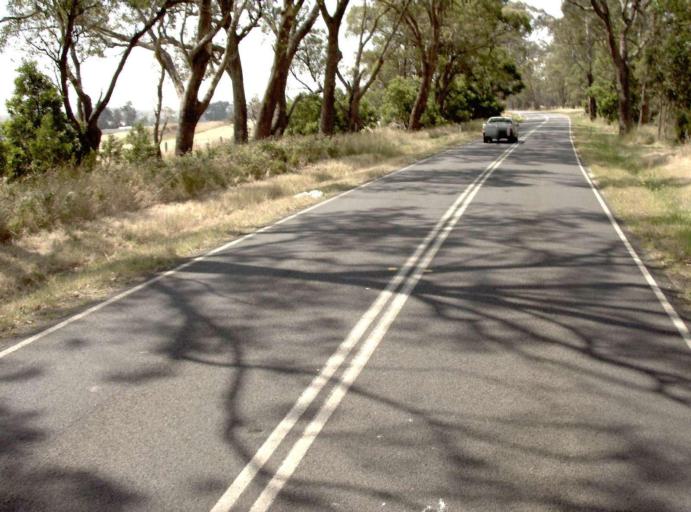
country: AU
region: Victoria
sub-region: Latrobe
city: Traralgon
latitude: -38.2695
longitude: 146.5463
